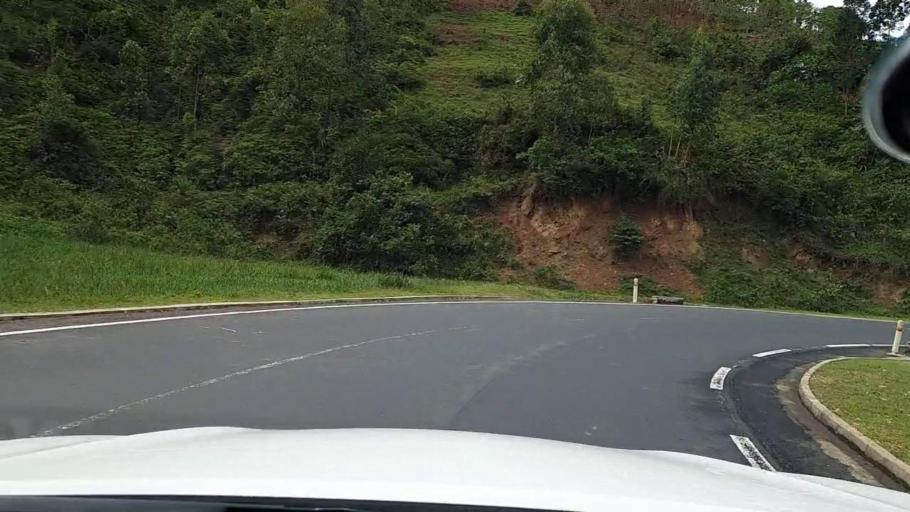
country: RW
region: Western Province
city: Kibuye
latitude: -2.1836
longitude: 29.2914
